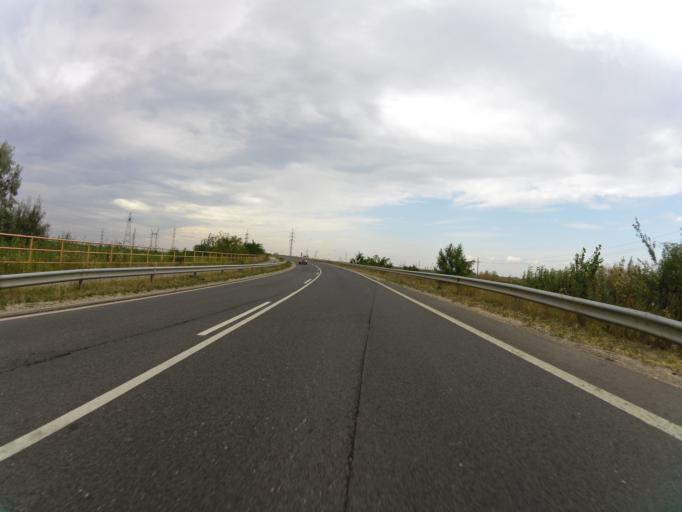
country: HU
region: Csongrad
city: Szeged
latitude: 46.2909
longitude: 20.1378
